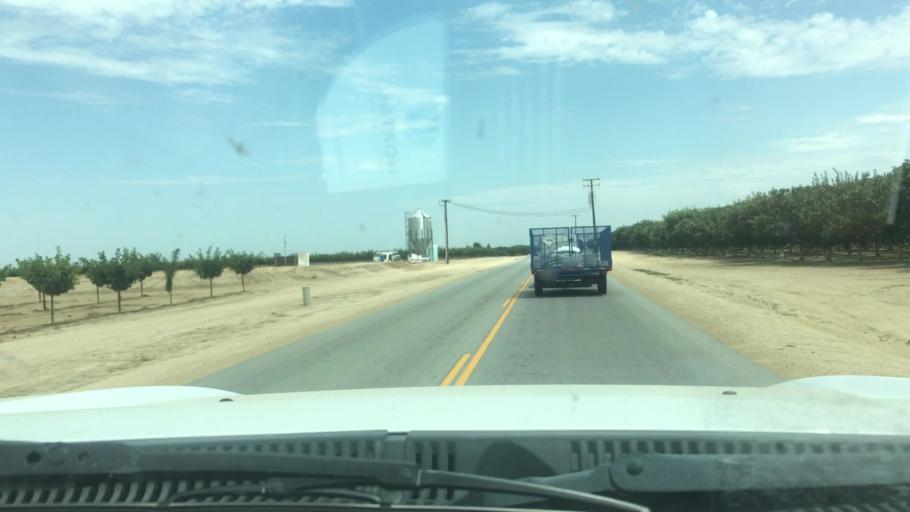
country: US
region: California
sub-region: Kern County
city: McFarland
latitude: 35.5898
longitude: -119.1510
